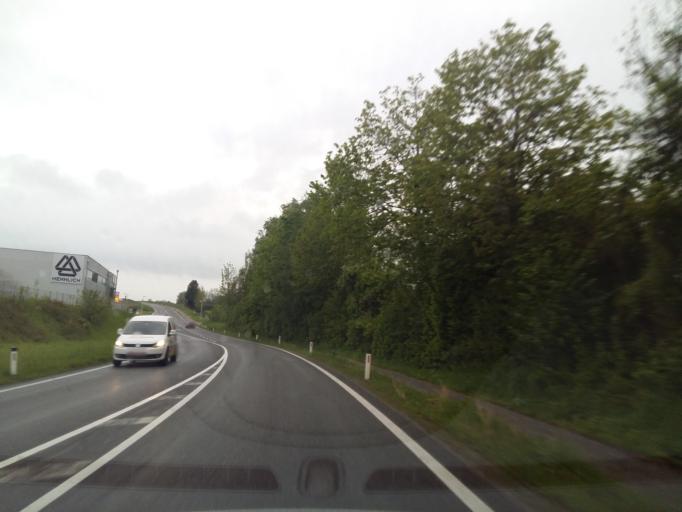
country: AT
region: Upper Austria
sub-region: Politischer Bezirk Scharding
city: Sankt Florian am Inn
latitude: 48.4202
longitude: 13.4376
